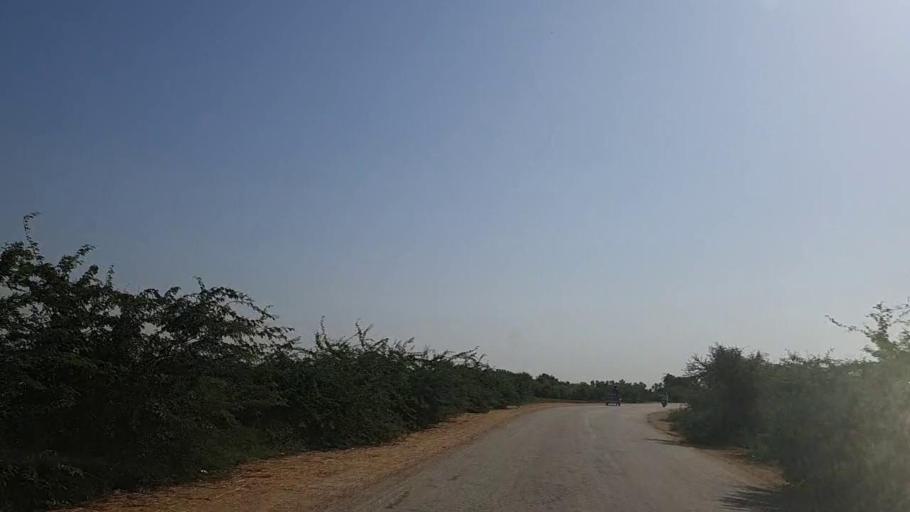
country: PK
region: Sindh
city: Mirpur Batoro
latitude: 24.6083
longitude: 68.2962
